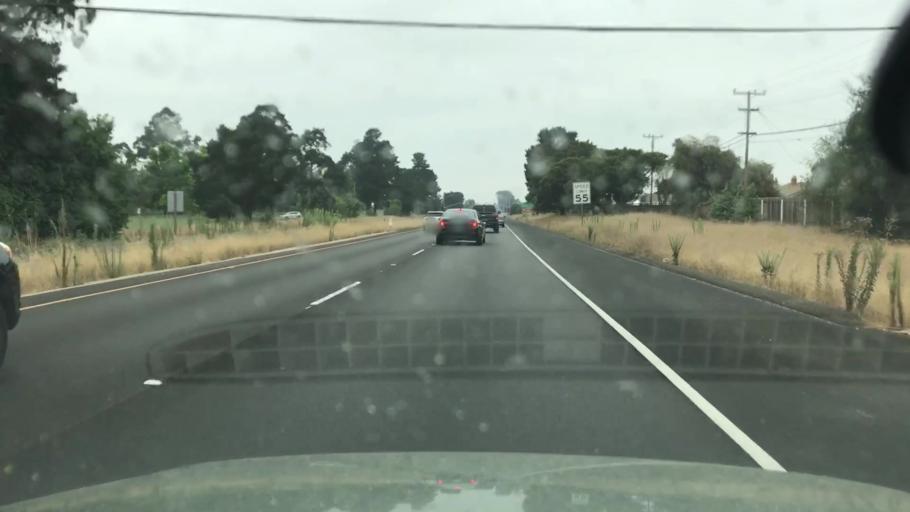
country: US
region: California
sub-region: Santa Barbara County
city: Orcutt
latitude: 34.9017
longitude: -120.4358
